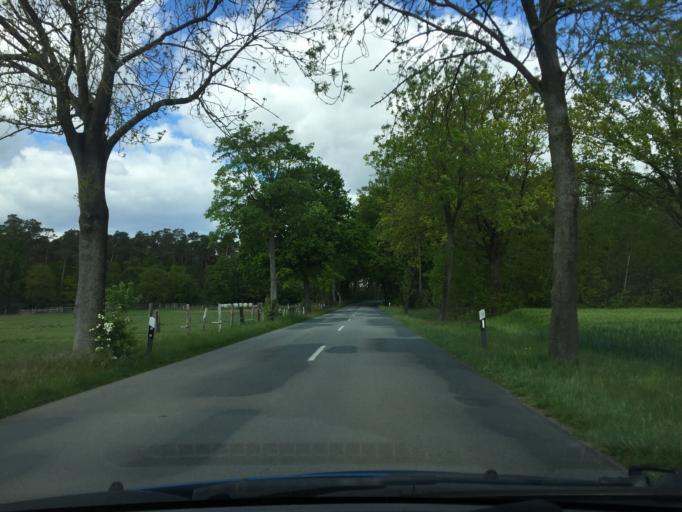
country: DE
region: Lower Saxony
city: Suderburg
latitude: 52.9232
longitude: 10.4986
